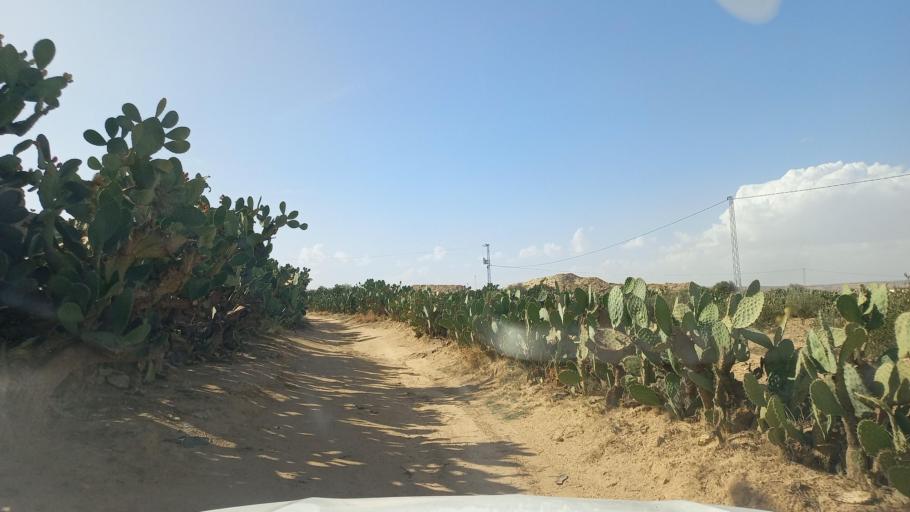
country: TN
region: Al Qasrayn
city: Sbiba
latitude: 35.3175
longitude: 9.0265
